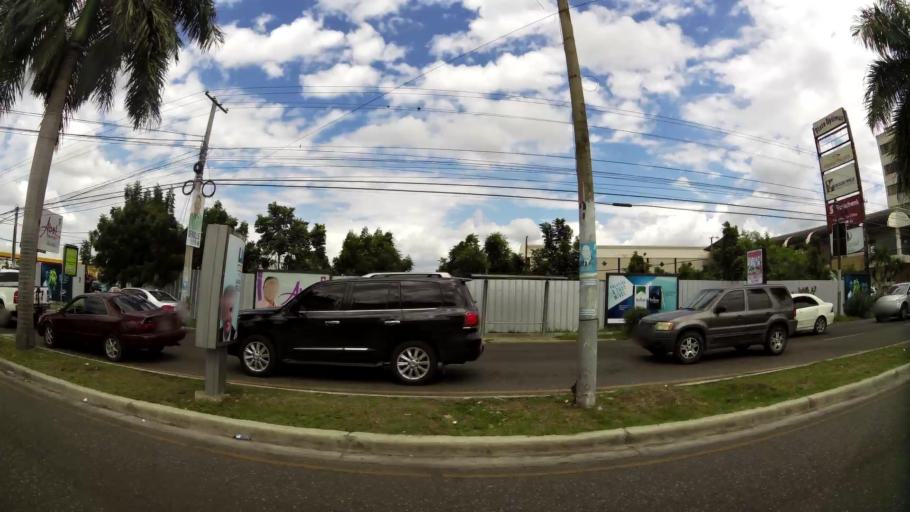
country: DO
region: Santiago
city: Santiago de los Caballeros
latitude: 19.4588
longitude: -70.6942
